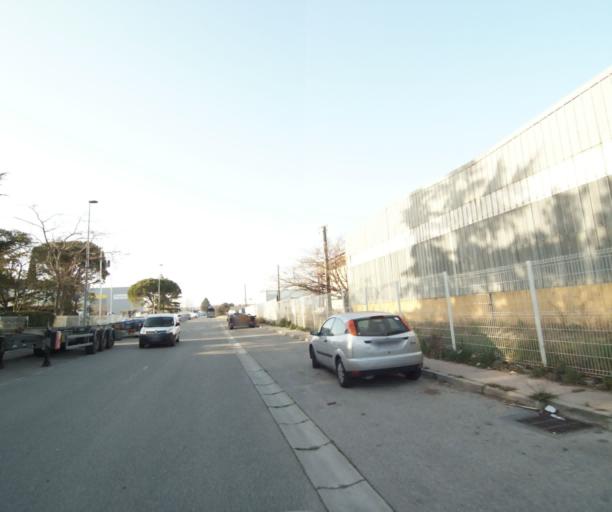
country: FR
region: Provence-Alpes-Cote d'Azur
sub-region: Departement des Bouches-du-Rhone
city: Saint-Victoret
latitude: 43.4285
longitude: 5.2457
